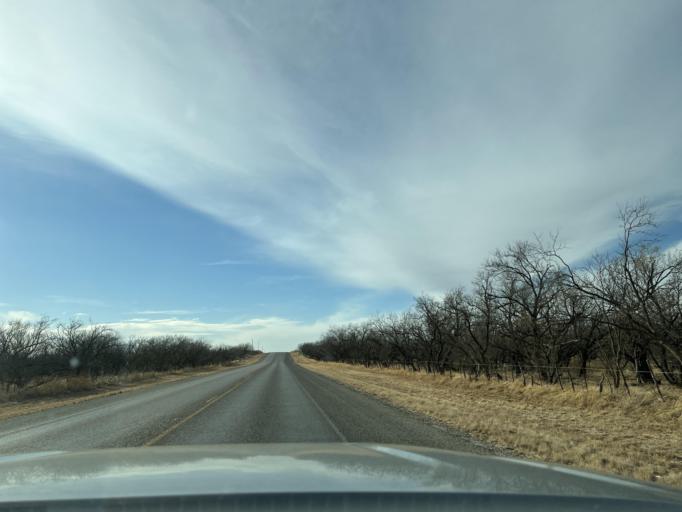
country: US
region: Texas
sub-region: Fisher County
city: Rotan
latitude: 32.7396
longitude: -100.5221
